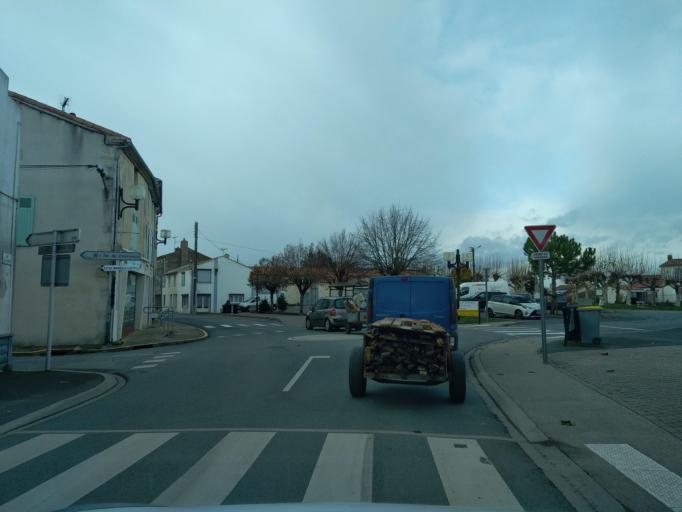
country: FR
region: Pays de la Loire
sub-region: Departement de la Vendee
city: Vix
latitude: 46.3639
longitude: -0.8585
